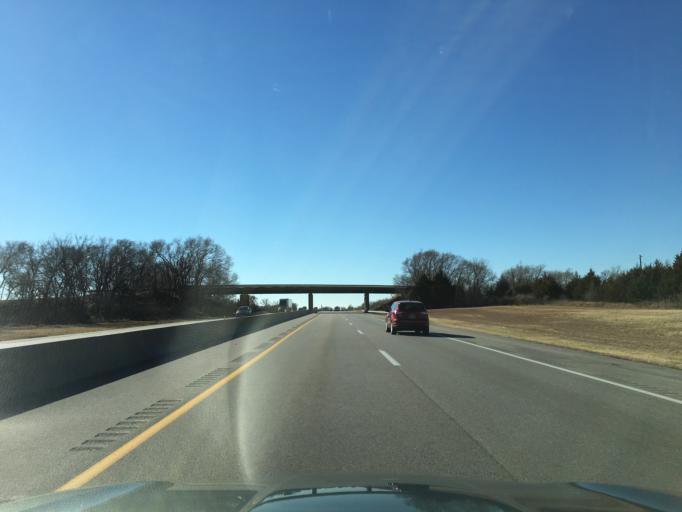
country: US
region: Kansas
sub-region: Sumner County
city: Belle Plaine
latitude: 37.3350
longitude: -97.3307
